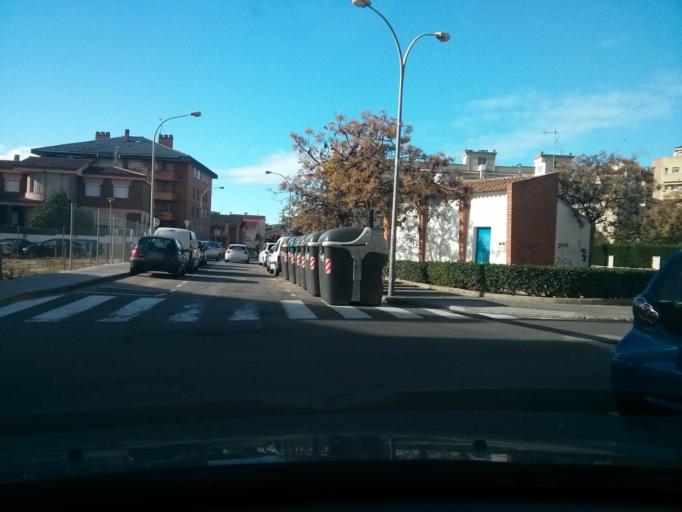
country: ES
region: Catalonia
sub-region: Provincia de Tarragona
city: El Vendrell
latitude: 41.2169
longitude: 1.5300
